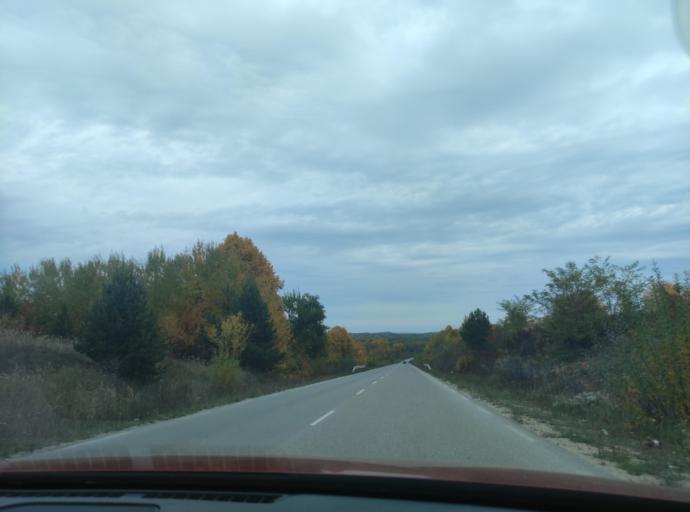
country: BG
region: Montana
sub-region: Obshtina Berkovitsa
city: Berkovitsa
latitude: 43.2290
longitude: 23.1578
